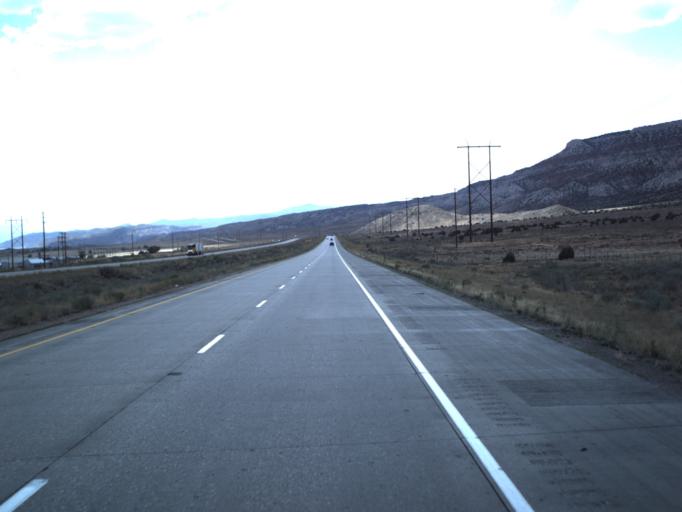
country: US
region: Utah
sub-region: Sevier County
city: Richfield
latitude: 38.8458
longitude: -112.0121
